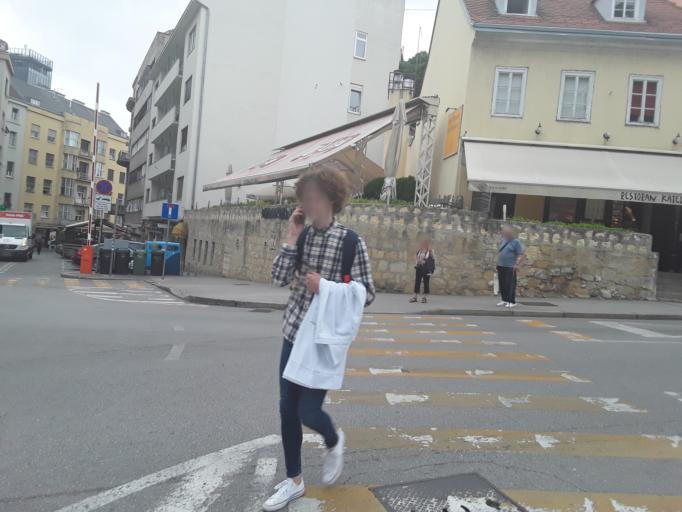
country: HR
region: Grad Zagreb
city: Zagreb
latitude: 45.8140
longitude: 15.9787
